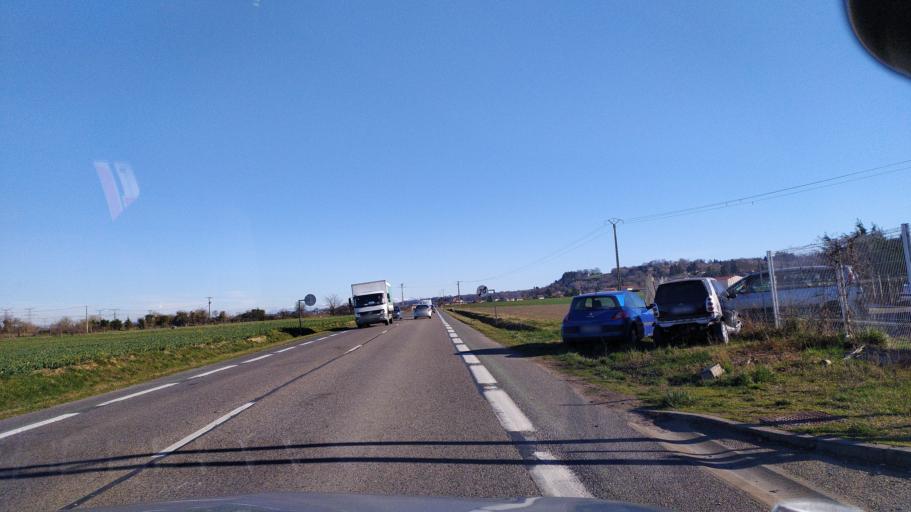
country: FR
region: Rhone-Alpes
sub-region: Departement du Rhone
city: Saint-Pierre-de-Chandieu
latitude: 45.6540
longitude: 5.0134
